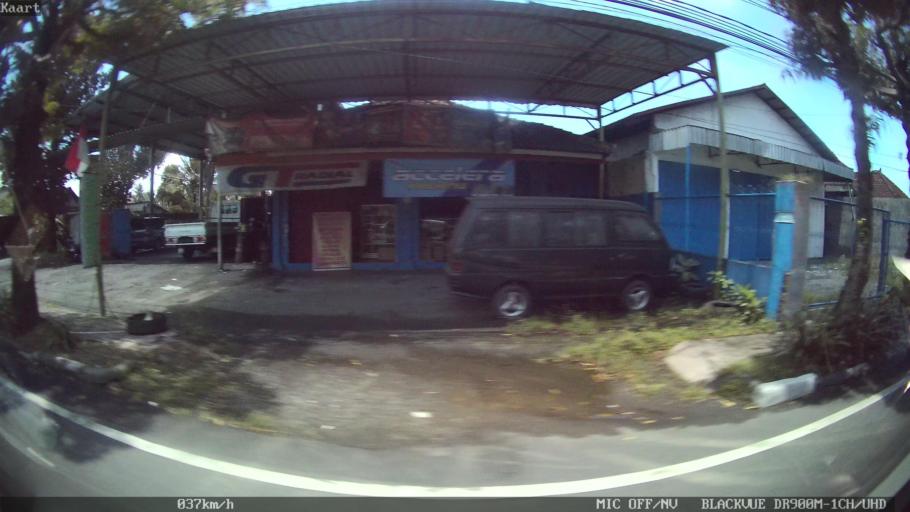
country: ID
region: Bali
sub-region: Kabupaten Gianyar
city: Ubud
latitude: -8.5554
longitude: 115.3025
